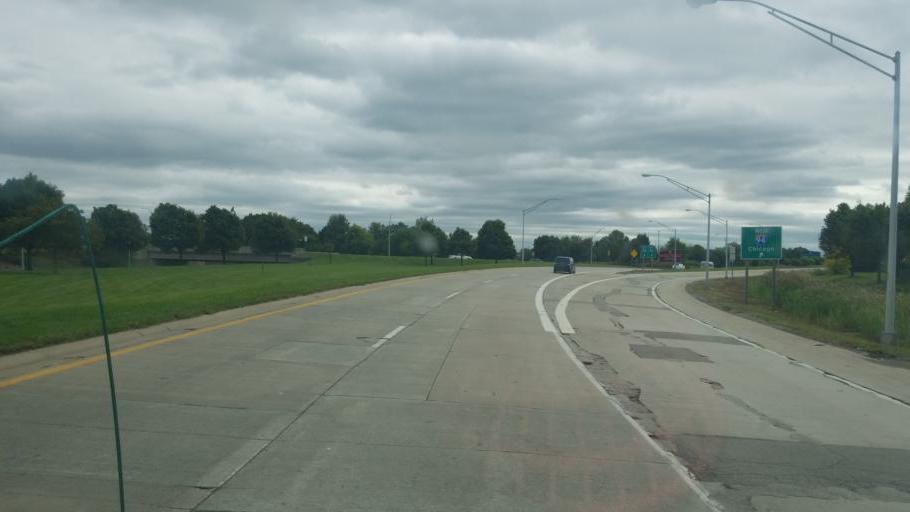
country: US
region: Michigan
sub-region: Wayne County
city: Romulus
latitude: 42.2422
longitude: -83.3440
